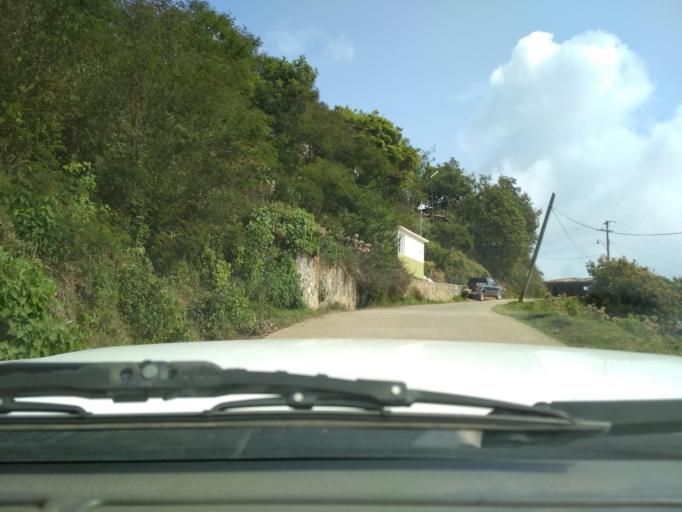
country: MX
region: Veracruz
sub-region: Camerino Z. Mendoza
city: Necoxtla
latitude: 18.7674
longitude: -97.1541
